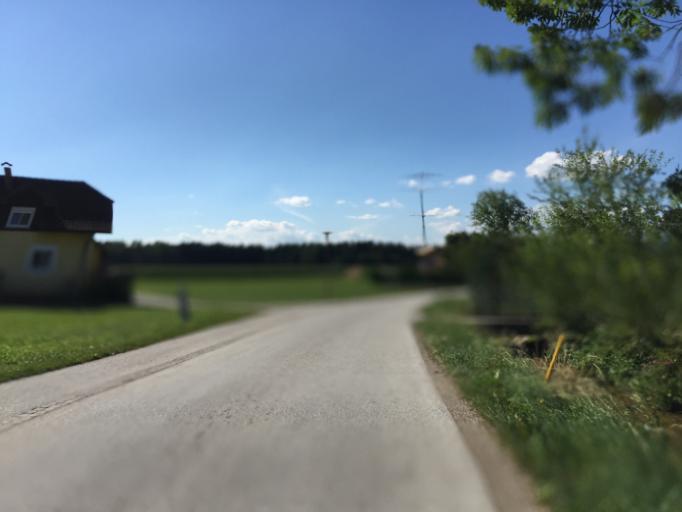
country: AT
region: Carinthia
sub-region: Politischer Bezirk Volkermarkt
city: Feistritz ob Bleiburg
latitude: 46.5651
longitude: 14.7559
